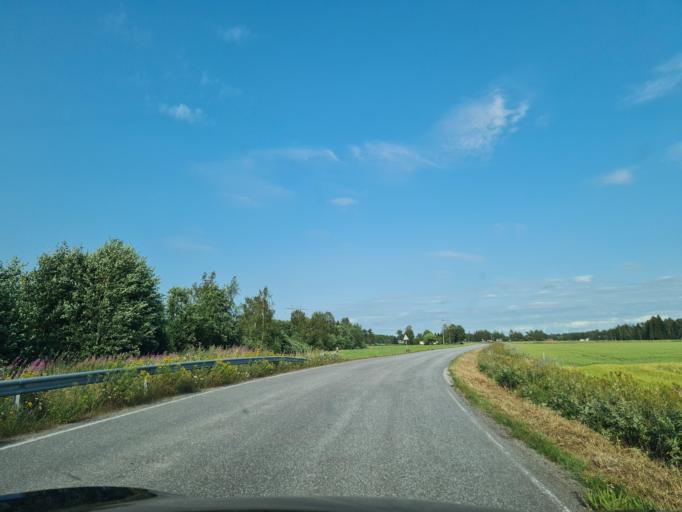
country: FI
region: Ostrobothnia
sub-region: Vaasa
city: Ristinummi
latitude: 63.0295
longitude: 21.8346
